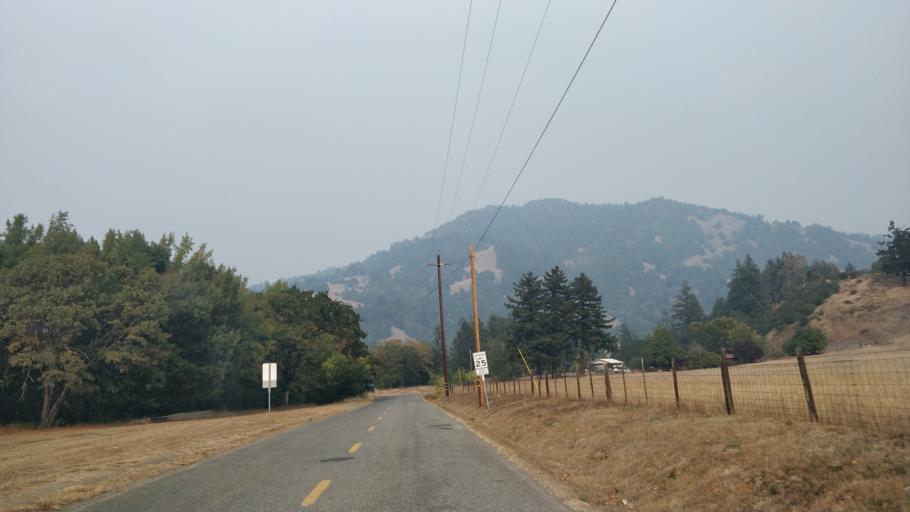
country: US
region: California
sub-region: Humboldt County
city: Rio Dell
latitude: 40.2409
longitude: -124.1305
